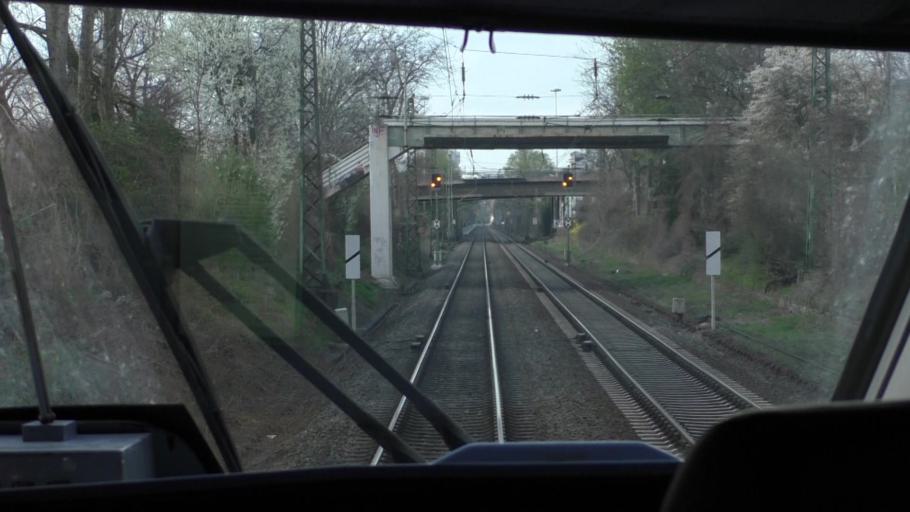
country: DE
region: North Rhine-Westphalia
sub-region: Regierungsbezirk Koln
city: Bonn
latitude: 50.7174
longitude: 7.1152
